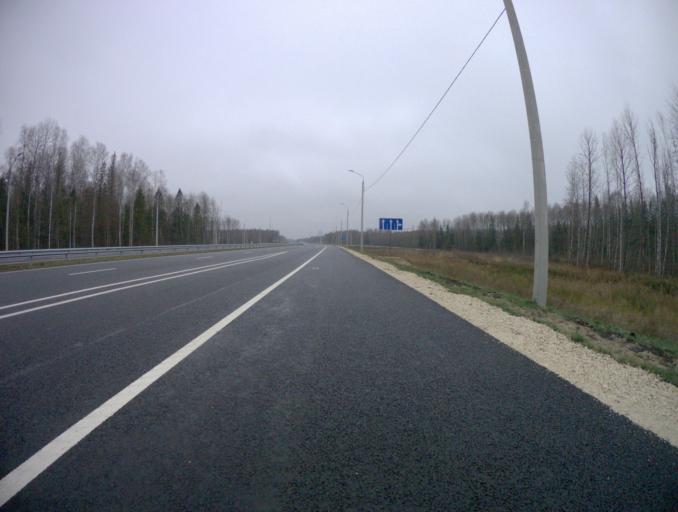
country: RU
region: Vladimir
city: Kommunar
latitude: 56.0414
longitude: 40.5239
